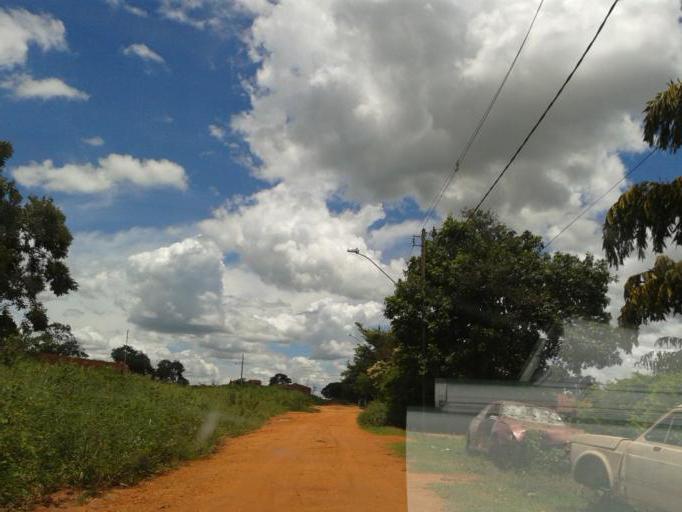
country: BR
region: Minas Gerais
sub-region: Santa Vitoria
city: Santa Vitoria
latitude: -18.8516
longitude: -50.1408
